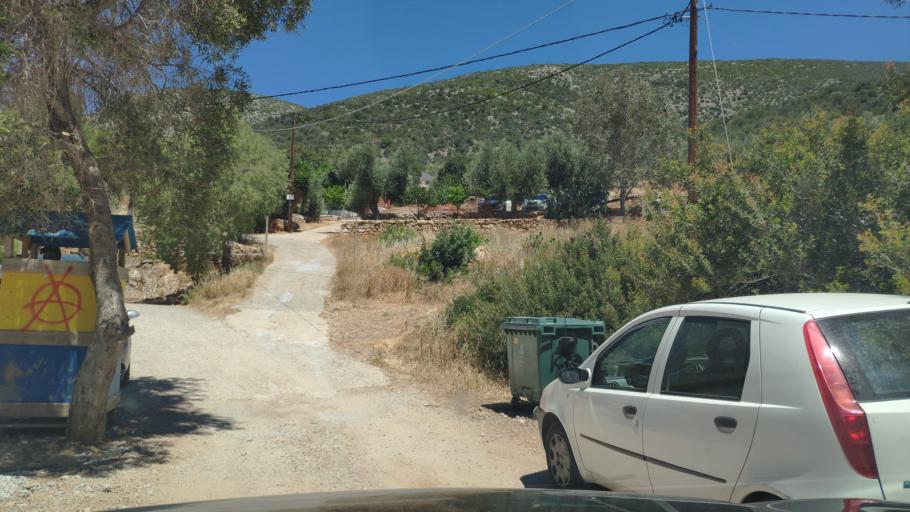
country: GR
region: Central Greece
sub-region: Nomos Voiotias
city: Kaparellion
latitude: 38.1833
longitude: 23.1430
